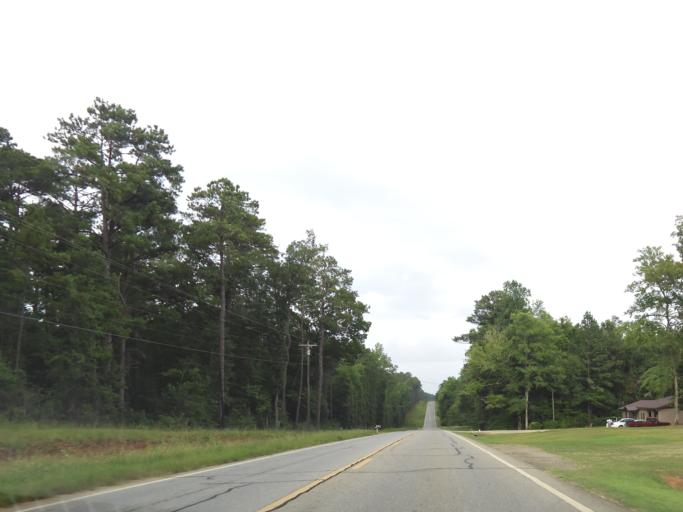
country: US
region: Georgia
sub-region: Bibb County
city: West Point
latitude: 32.8658
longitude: -83.8287
